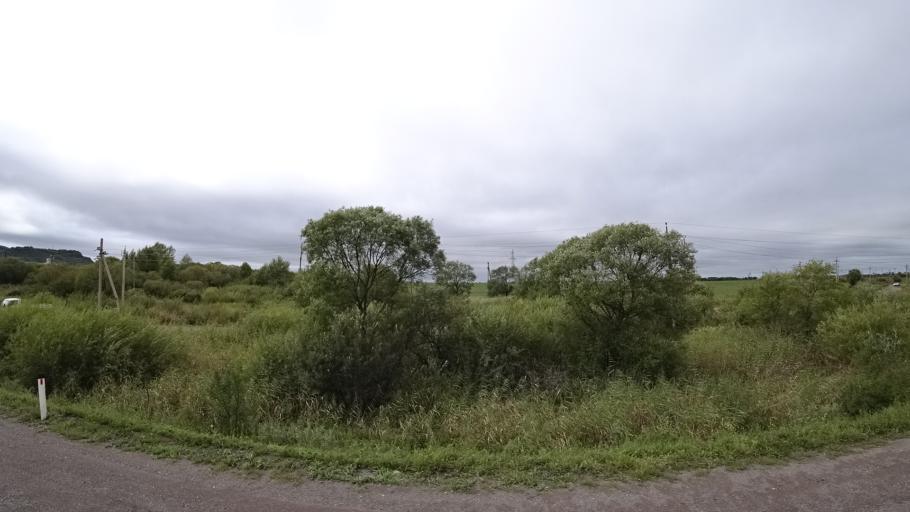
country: RU
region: Primorskiy
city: Monastyrishche
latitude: 44.1767
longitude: 132.4413
